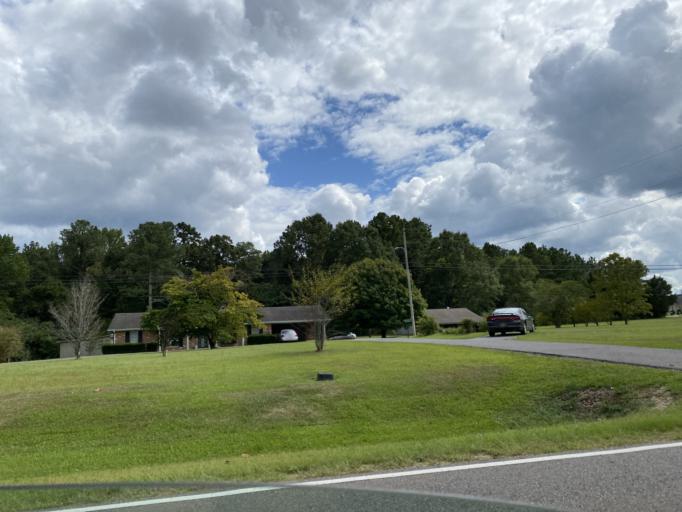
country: US
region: Mississippi
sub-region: Monroe County
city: Amory
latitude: 33.9755
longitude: -88.4328
